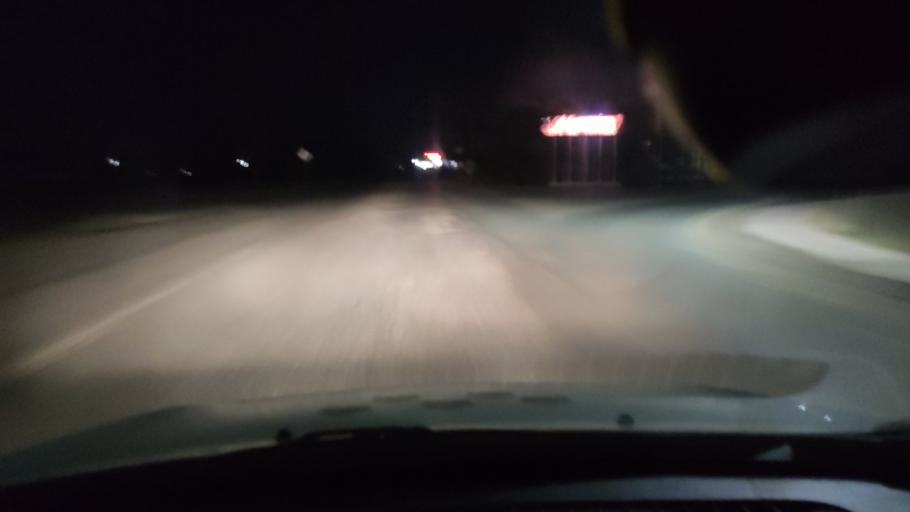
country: RU
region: Samara
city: Podstepki
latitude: 53.5724
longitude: 49.0838
